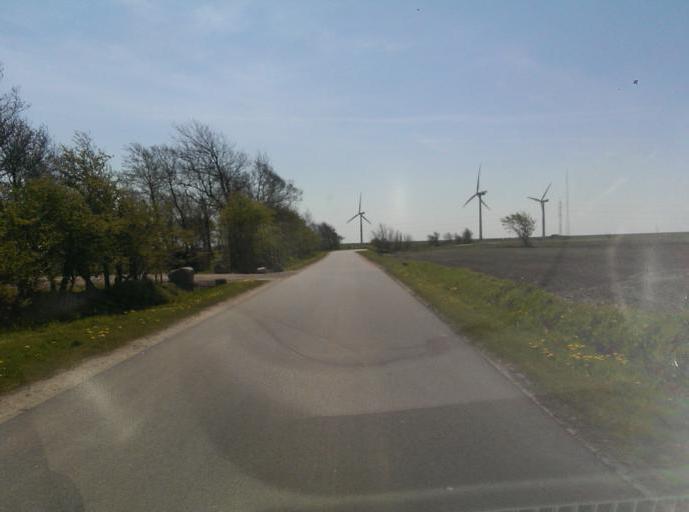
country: DK
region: South Denmark
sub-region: Esbjerg Kommune
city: Tjaereborg
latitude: 55.4561
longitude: 8.5932
